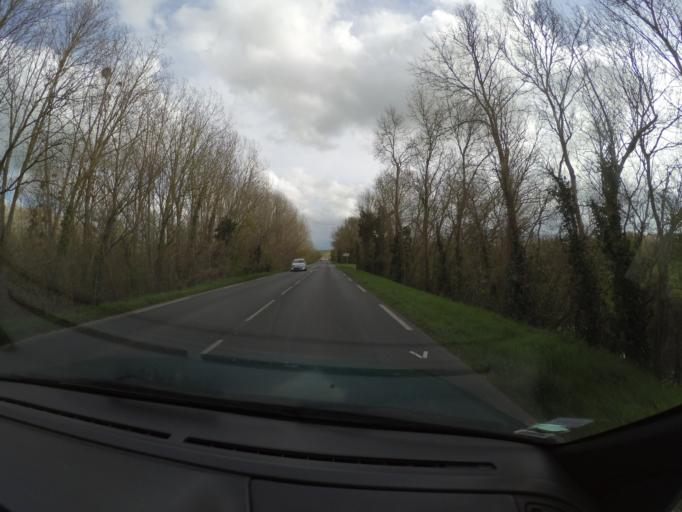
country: FR
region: Pays de la Loire
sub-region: Departement de Maine-et-Loire
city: Lire
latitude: 47.3514
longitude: -1.1683
